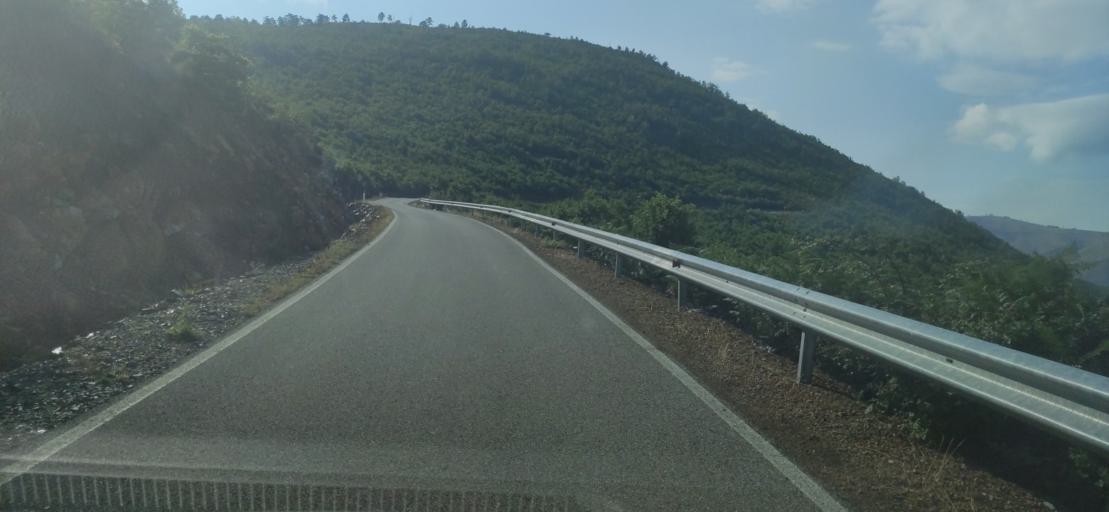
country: AL
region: Shkoder
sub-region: Rrethi i Pukes
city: Iballe
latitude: 42.1715
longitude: 20.0012
